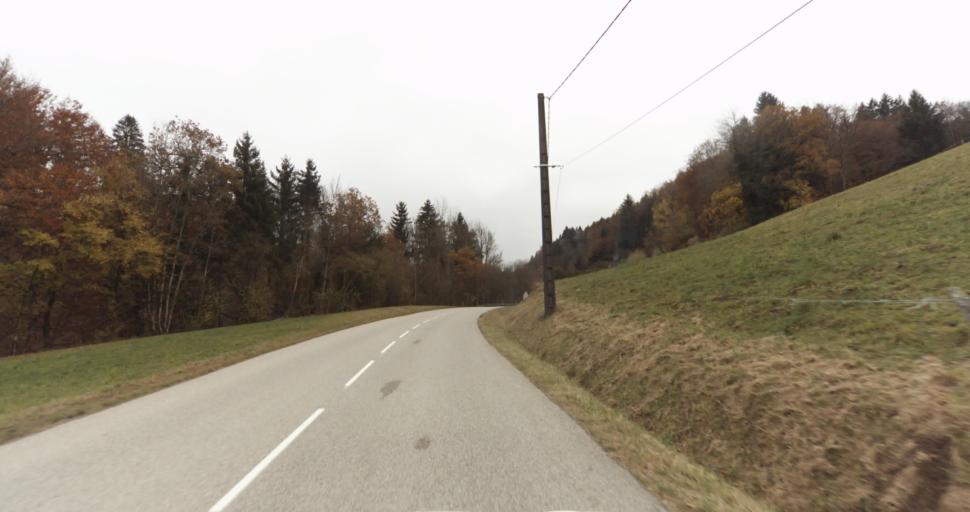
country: FR
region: Rhone-Alpes
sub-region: Departement de la Haute-Savoie
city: Saint-Jorioz
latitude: 45.8075
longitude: 6.1444
